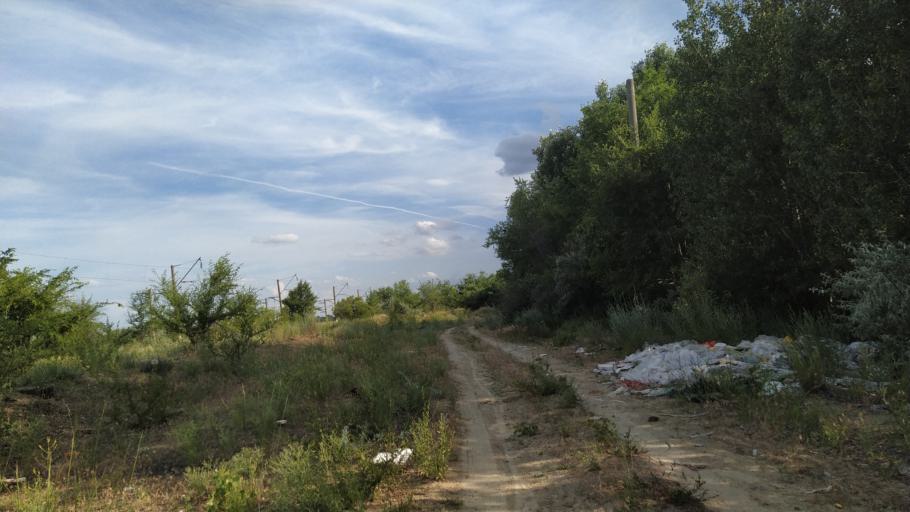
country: RU
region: Rostov
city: Bataysk
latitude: 47.1196
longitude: 39.7130
